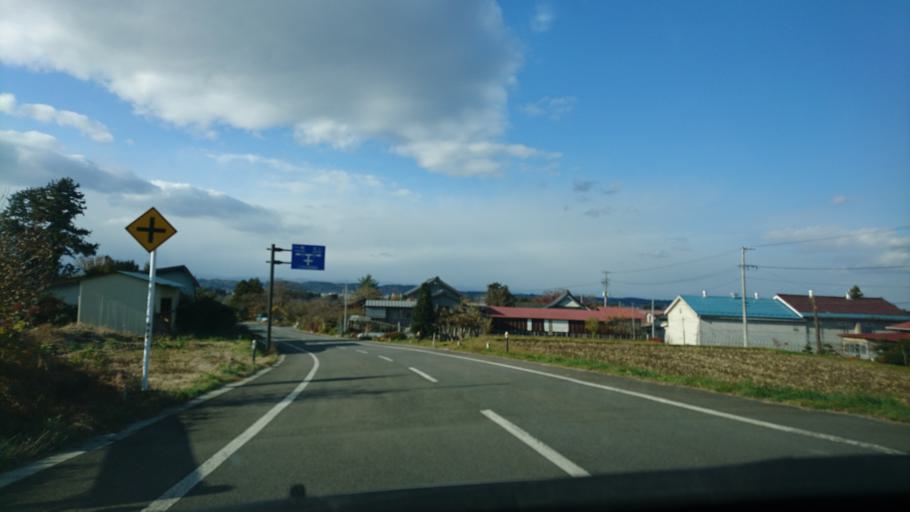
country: JP
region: Iwate
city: Mizusawa
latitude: 39.0348
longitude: 141.1537
